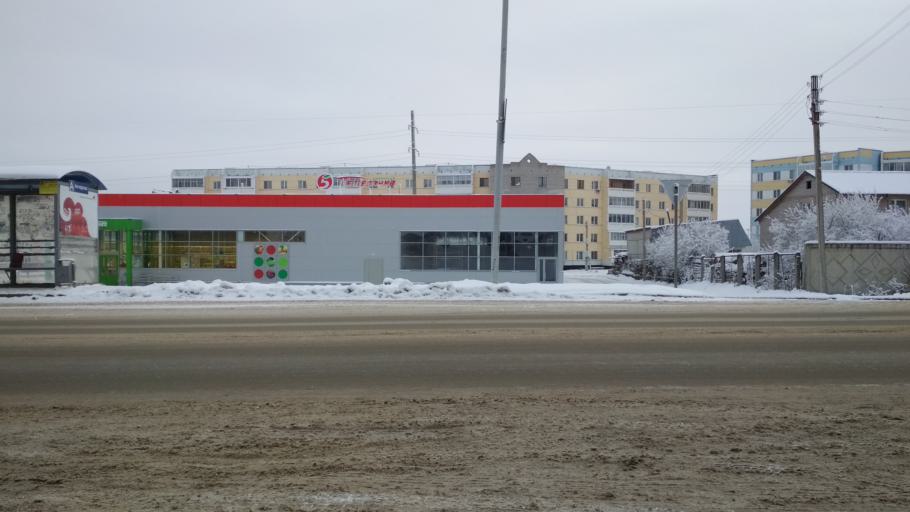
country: RU
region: Tatarstan
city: Zainsk
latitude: 55.2983
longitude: 51.9960
